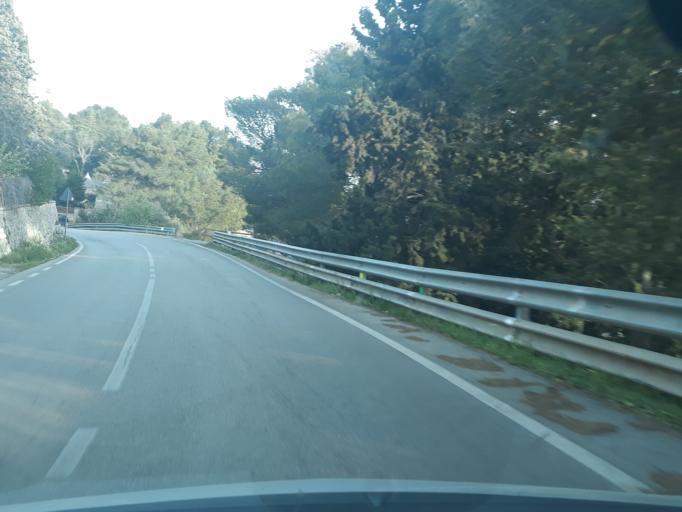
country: IT
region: Apulia
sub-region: Provincia di Brindisi
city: Lamie di Olimpie-Selva
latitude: 40.8230
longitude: 17.3260
